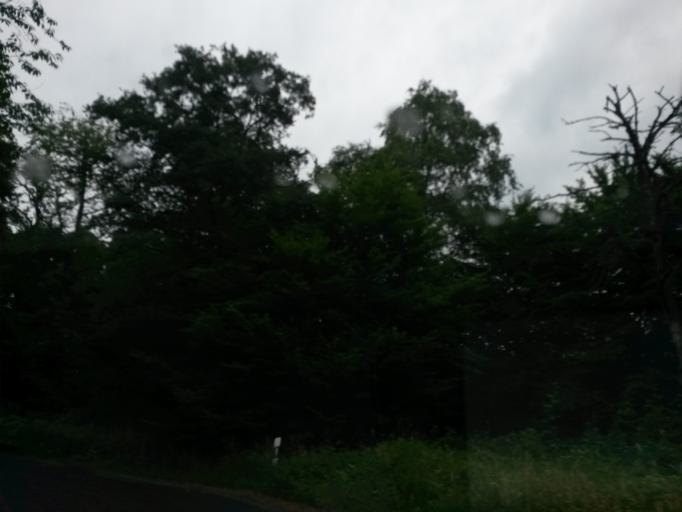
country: DE
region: North Rhine-Westphalia
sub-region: Regierungsbezirk Koln
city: Much
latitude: 50.9469
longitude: 7.3663
